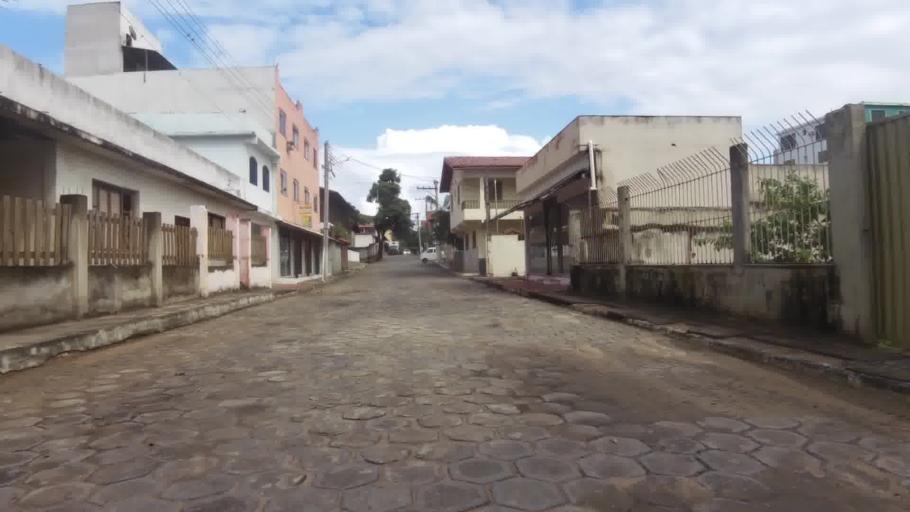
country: BR
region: Espirito Santo
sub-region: Piuma
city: Piuma
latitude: -20.8323
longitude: -40.6944
